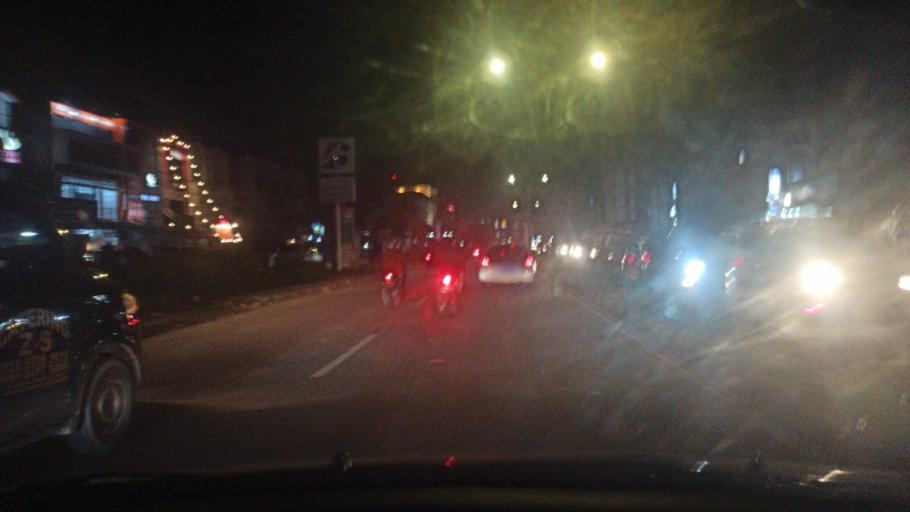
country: ID
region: South Sumatra
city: Palembang
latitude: -2.9522
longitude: 104.7569
